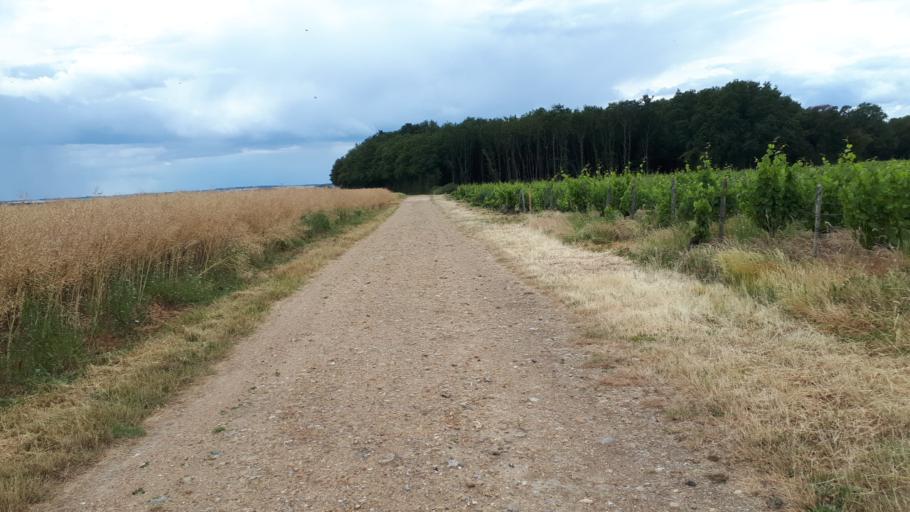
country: FR
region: Centre
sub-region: Departement du Loir-et-Cher
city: Villiers-sur-Loir
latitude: 47.8062
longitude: 1.0113
